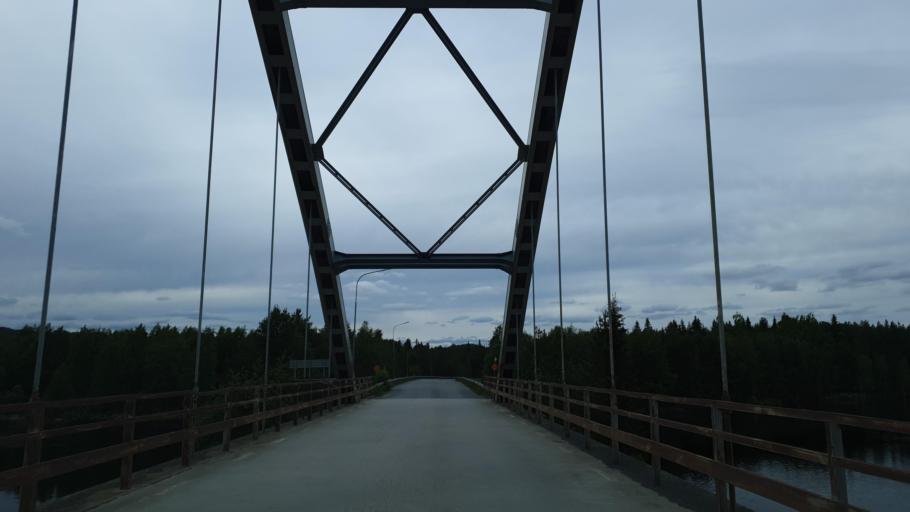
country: SE
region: Vaesterbotten
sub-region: Sorsele Kommun
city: Sorsele
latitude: 65.5428
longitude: 17.5105
